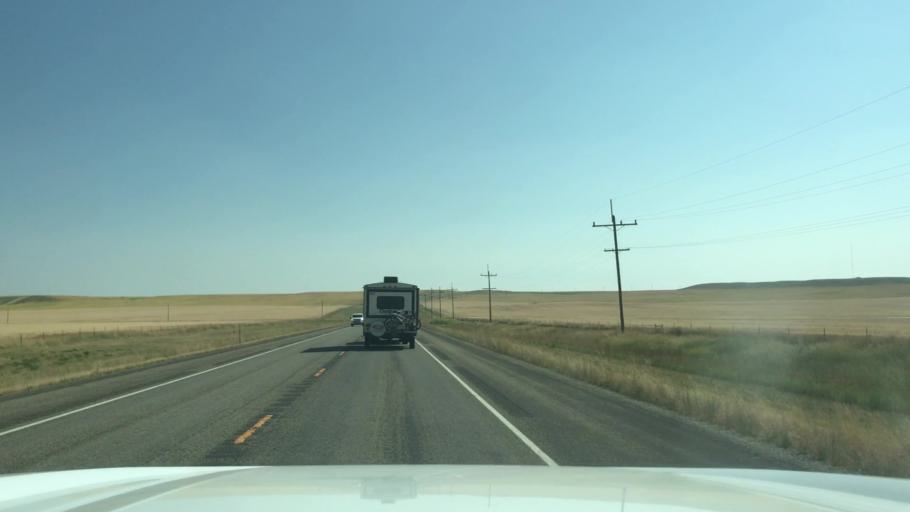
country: US
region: Montana
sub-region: Wheatland County
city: Harlowton
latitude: 46.4834
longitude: -109.7661
